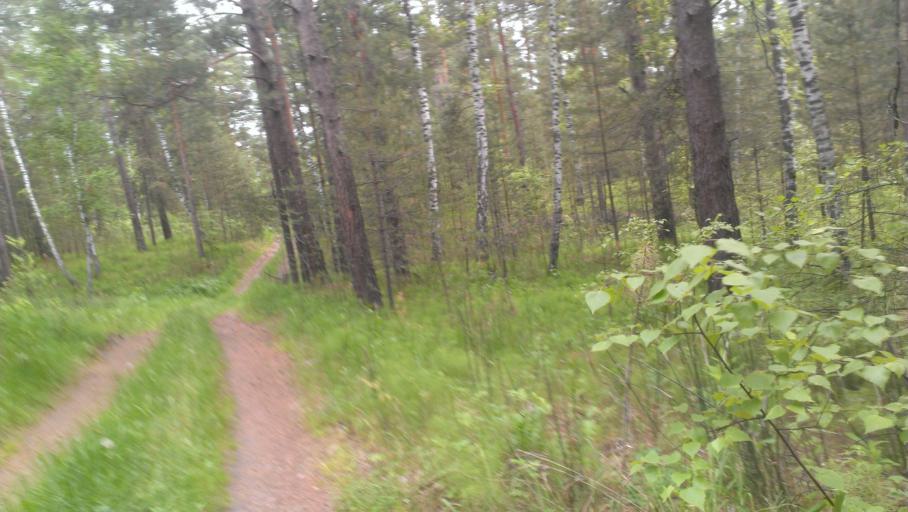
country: RU
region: Altai Krai
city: Sannikovo
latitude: 53.3493
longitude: 84.0376
